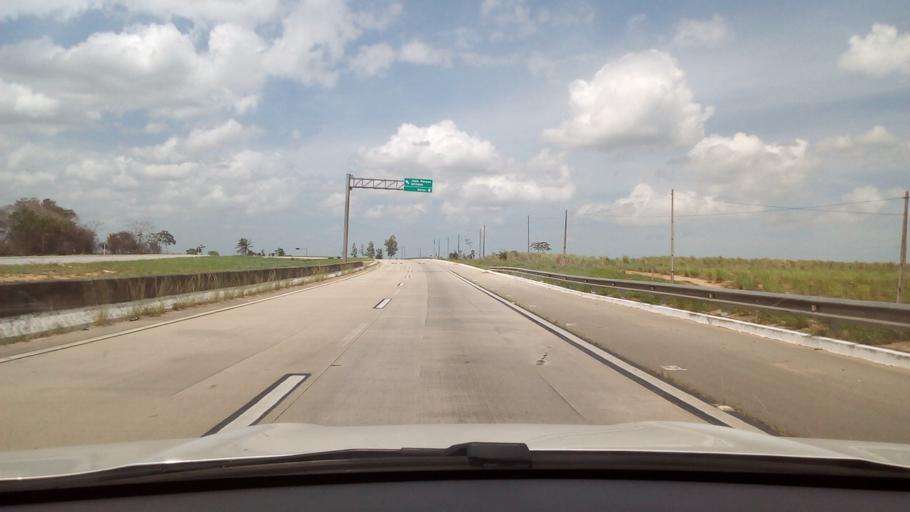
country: BR
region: Paraiba
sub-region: Mamanguape
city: Mamanguape
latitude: -6.7905
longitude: -35.1356
